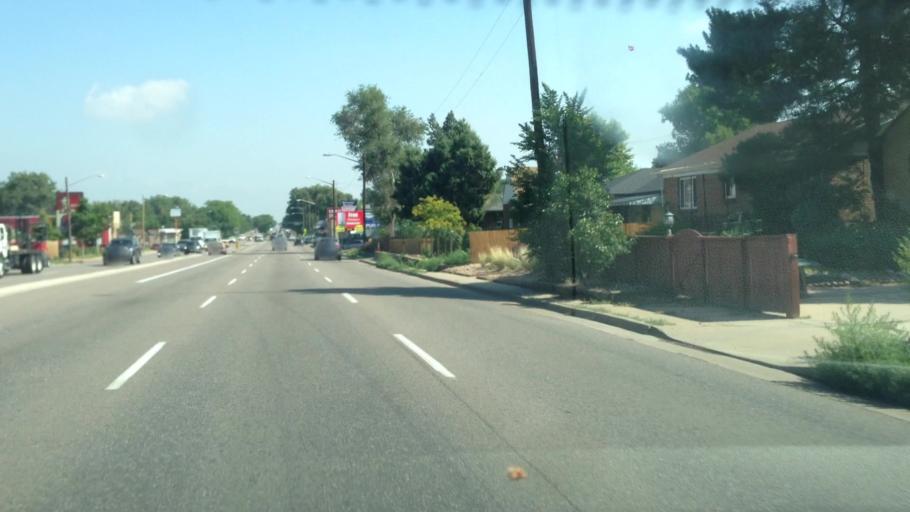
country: US
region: Colorado
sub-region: Denver County
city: Denver
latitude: 39.7554
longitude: -104.9405
